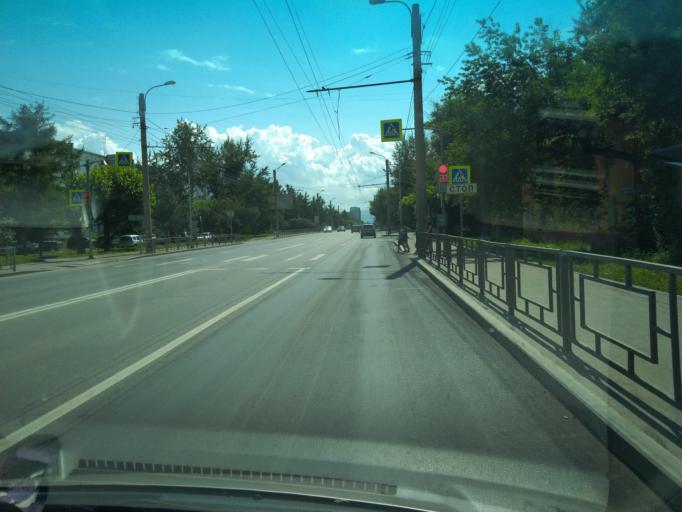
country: RU
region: Krasnoyarskiy
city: Solnechnyy
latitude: 56.0525
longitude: 92.9412
